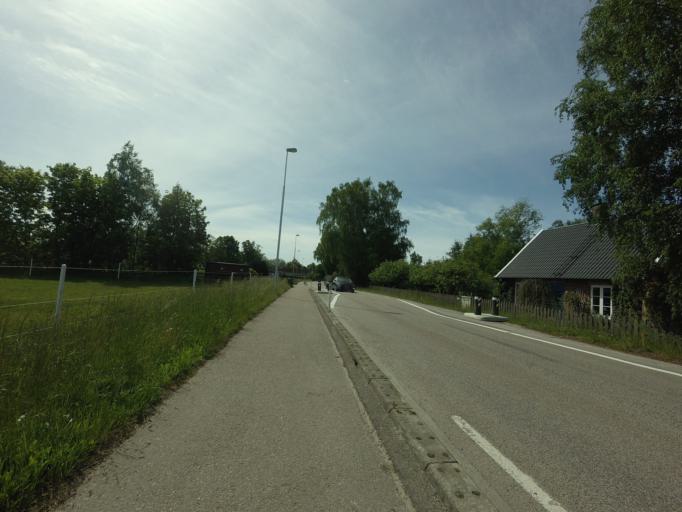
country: SE
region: Skane
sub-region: Helsingborg
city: Odakra
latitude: 56.1283
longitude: 12.6939
